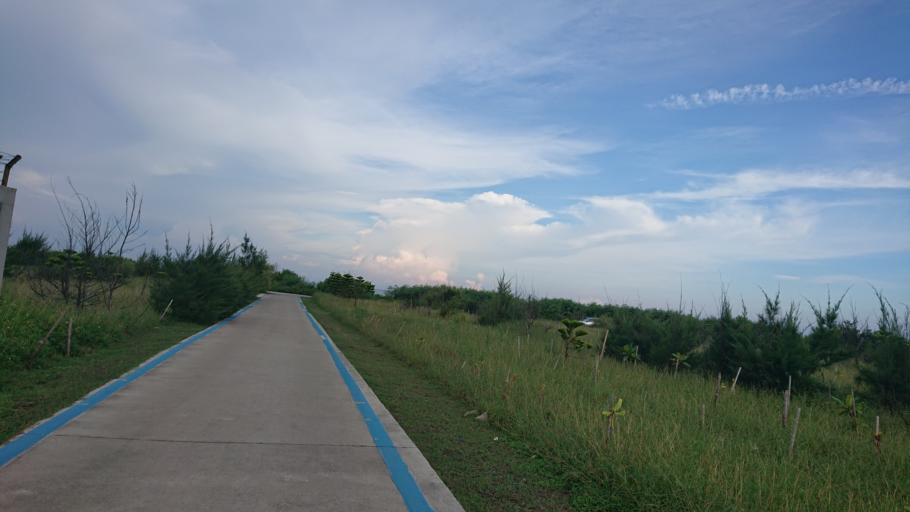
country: TW
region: Taiwan
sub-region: Penghu
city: Ma-kung
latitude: 23.5208
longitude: 119.6101
